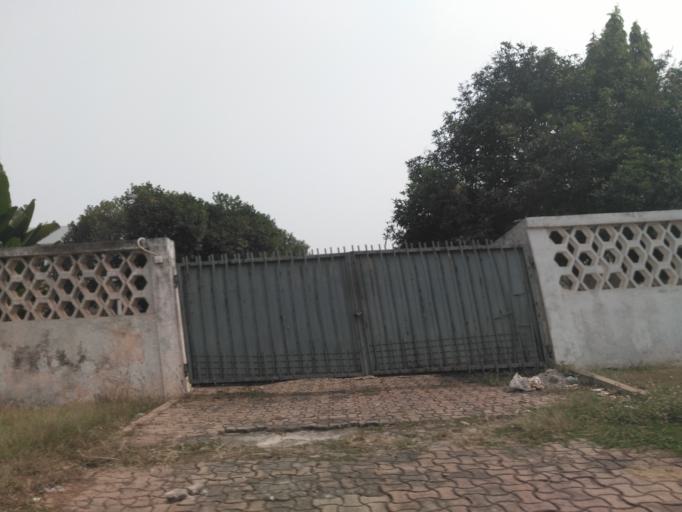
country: GH
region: Ashanti
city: Kumasi
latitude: 6.6769
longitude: -1.6326
